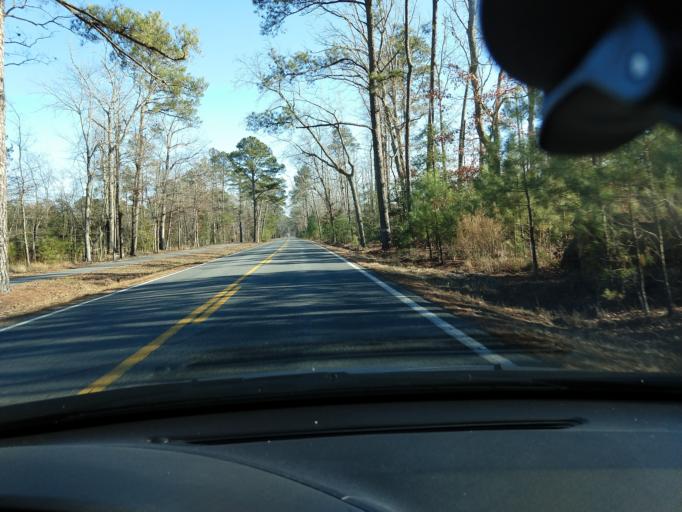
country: US
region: Virginia
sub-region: Charles City County
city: Charles City
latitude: 37.2943
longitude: -76.9383
